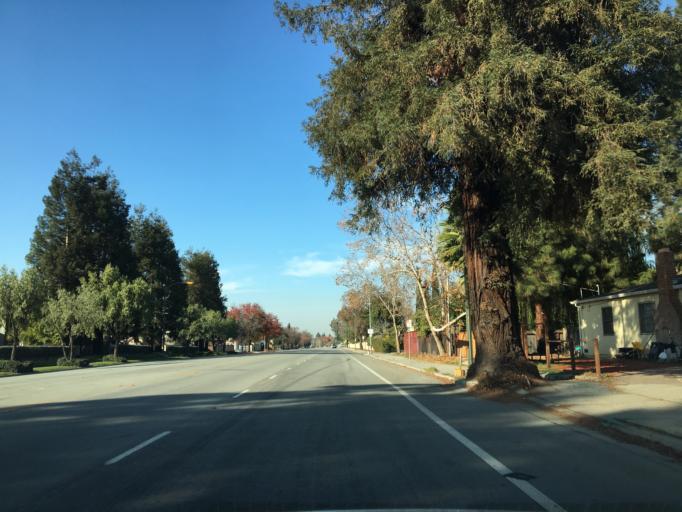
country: US
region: California
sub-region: Santa Clara County
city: San Jose
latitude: 37.3753
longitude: -121.8743
